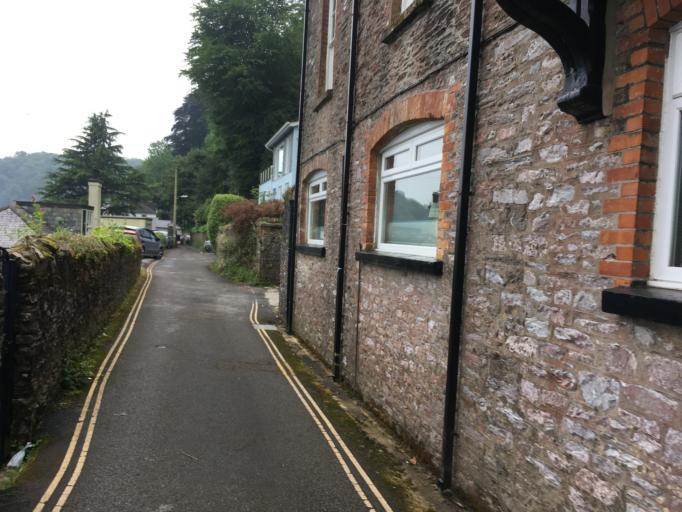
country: GB
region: England
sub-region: Devon
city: Dartmouth
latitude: 50.3453
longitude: -3.5773
